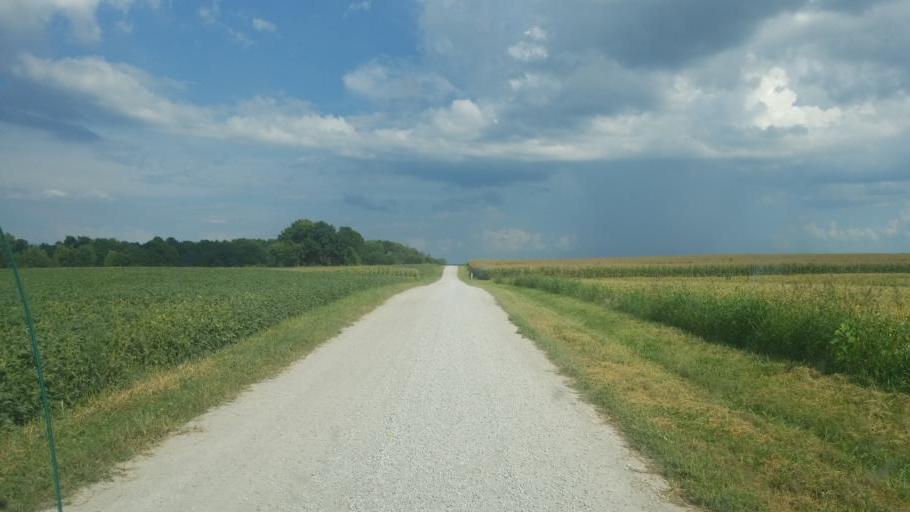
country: US
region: Ohio
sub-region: Huron County
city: Willard
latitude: 40.9960
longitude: -82.7840
